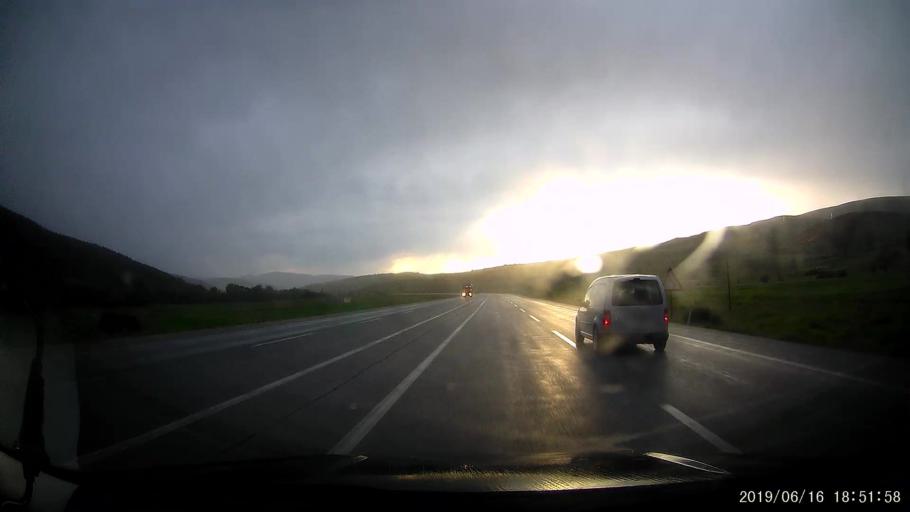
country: TR
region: Erzincan
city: Catalcam
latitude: 39.9023
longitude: 38.9137
